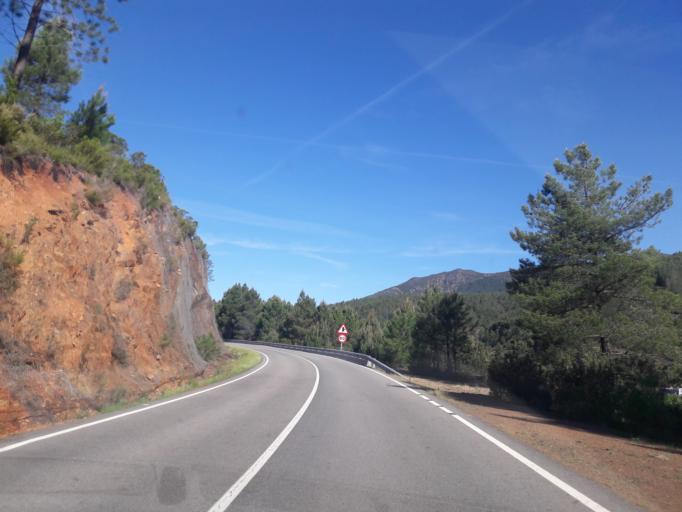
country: ES
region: Castille and Leon
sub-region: Provincia de Salamanca
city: Herguijuela de la Sierra
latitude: 40.4112
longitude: -6.0961
